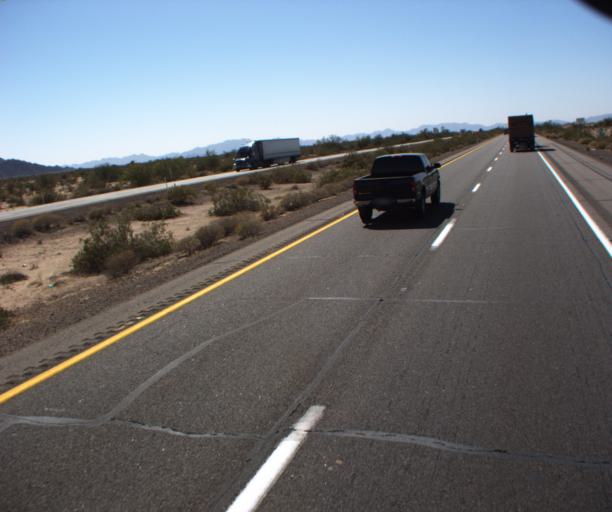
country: US
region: Arizona
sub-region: Yuma County
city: Wellton
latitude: 32.6911
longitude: -113.9705
